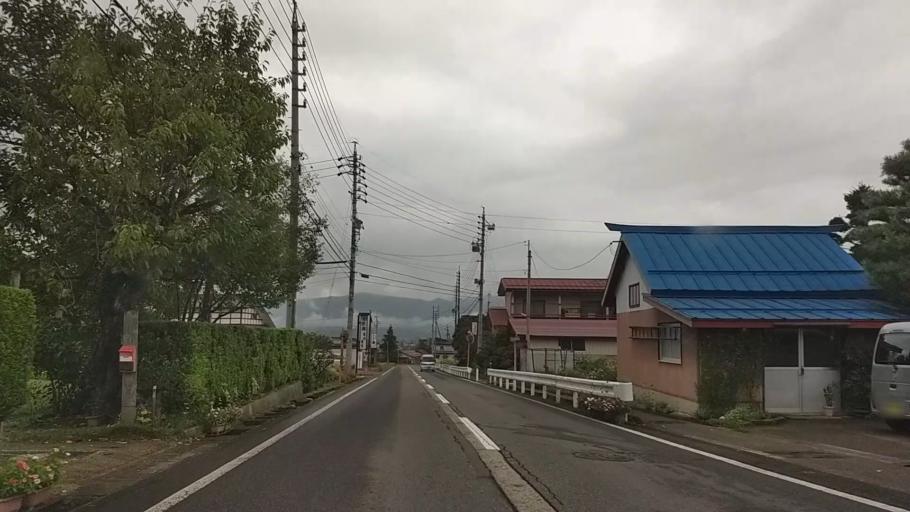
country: JP
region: Nagano
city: Iiyama
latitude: 36.8401
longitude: 138.4074
